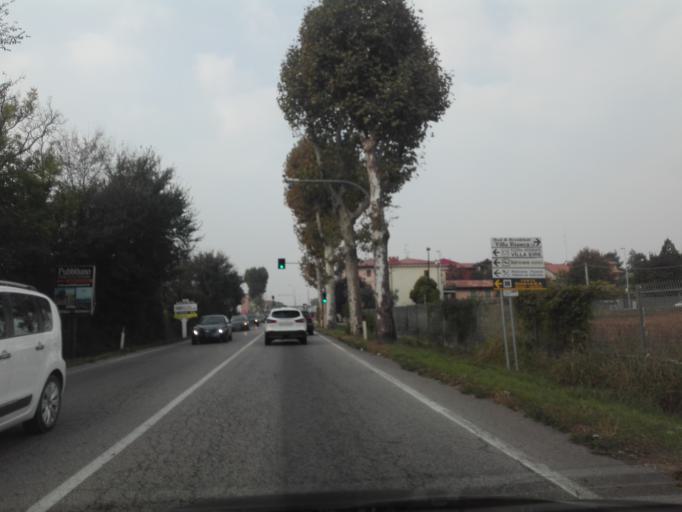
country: IT
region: Veneto
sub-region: Provincia di Verona
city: Sona
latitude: 45.4437
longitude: 10.8227
